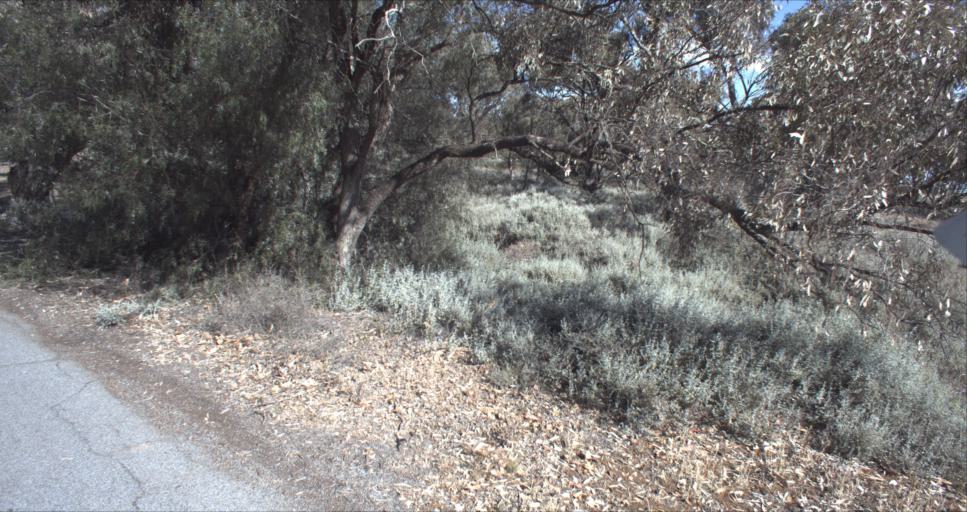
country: AU
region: New South Wales
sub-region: Leeton
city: Leeton
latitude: -34.5586
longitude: 146.3866
